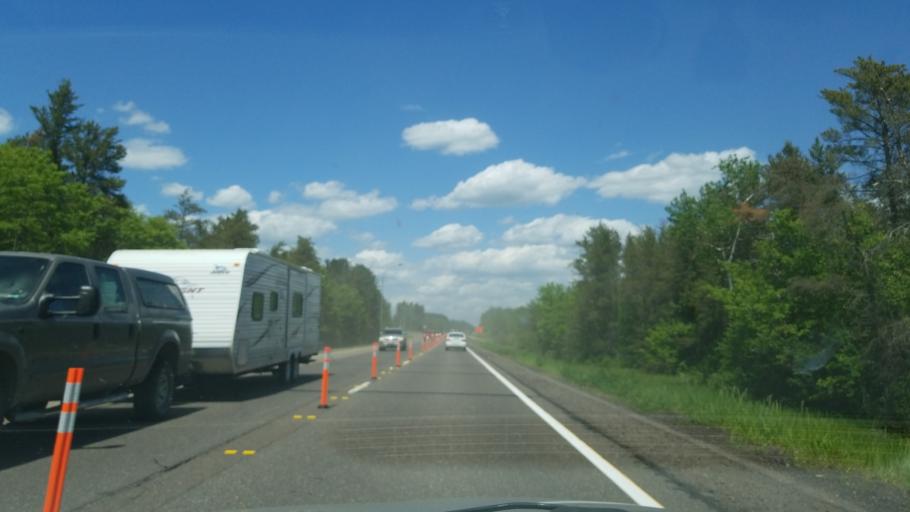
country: US
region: Minnesota
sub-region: Carlton County
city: Moose Lake
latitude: 46.3513
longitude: -92.8086
